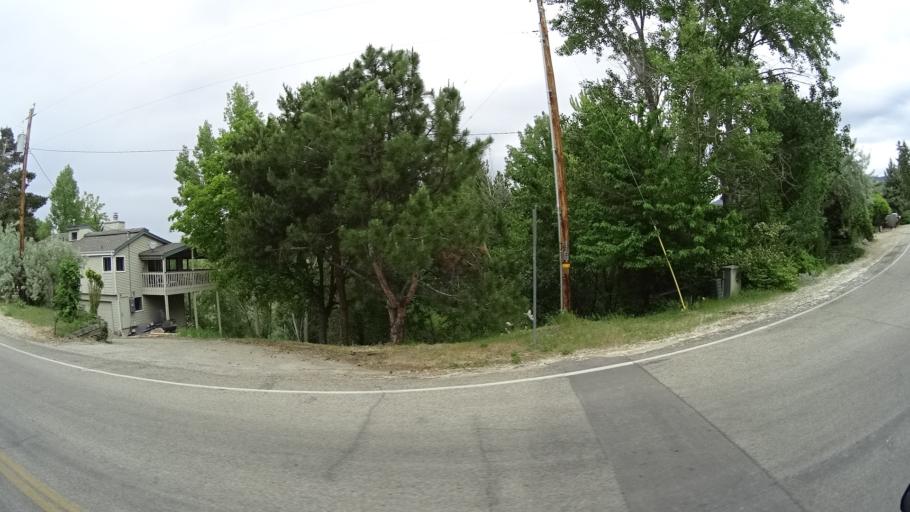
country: US
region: Idaho
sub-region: Ada County
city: Boise
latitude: 43.6172
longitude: -116.1690
